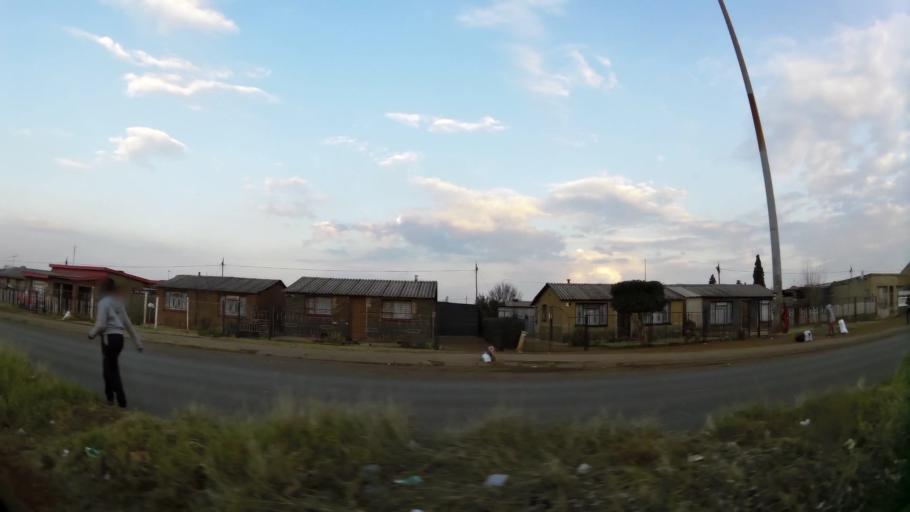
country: ZA
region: Gauteng
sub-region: City of Johannesburg Metropolitan Municipality
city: Orange Farm
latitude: -26.5681
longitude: 27.8478
